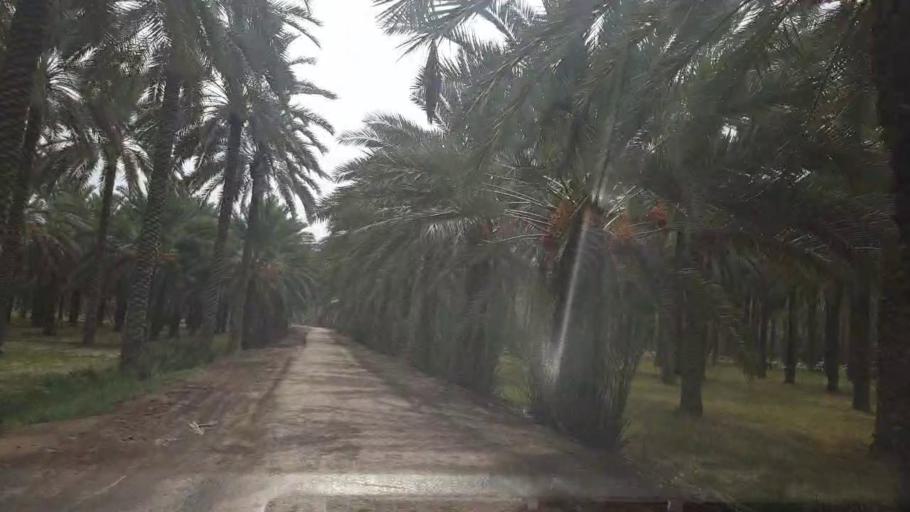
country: PK
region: Sindh
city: Khairpur
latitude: 27.6063
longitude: 68.8069
